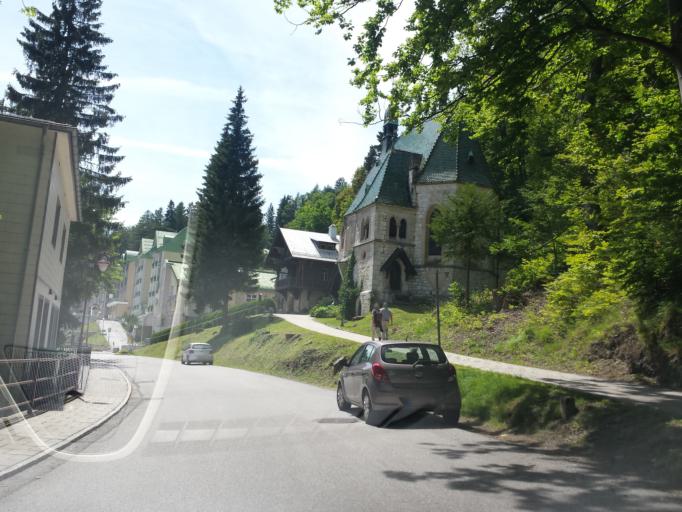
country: AT
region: Lower Austria
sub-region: Politischer Bezirk Neunkirchen
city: Semmering
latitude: 47.6393
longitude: 15.8259
